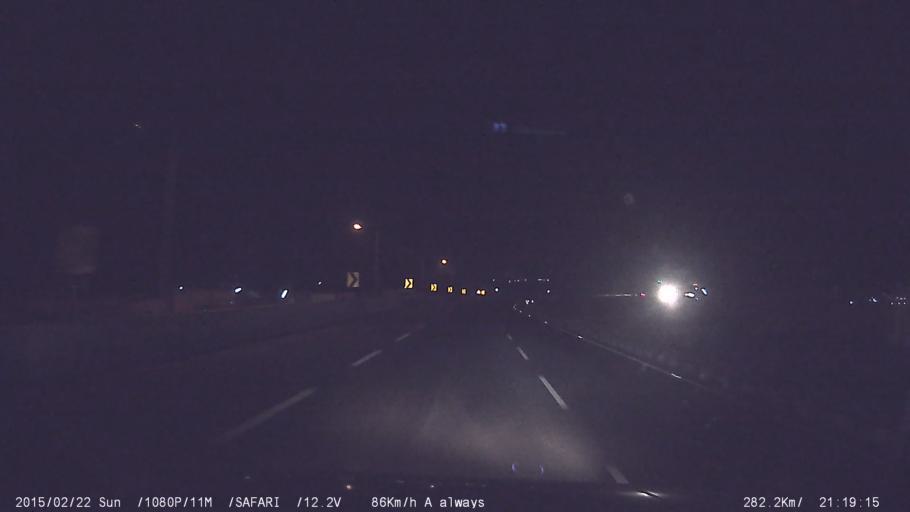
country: IN
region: Tamil Nadu
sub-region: Karur
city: Pallappatti
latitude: 10.8465
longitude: 77.9712
